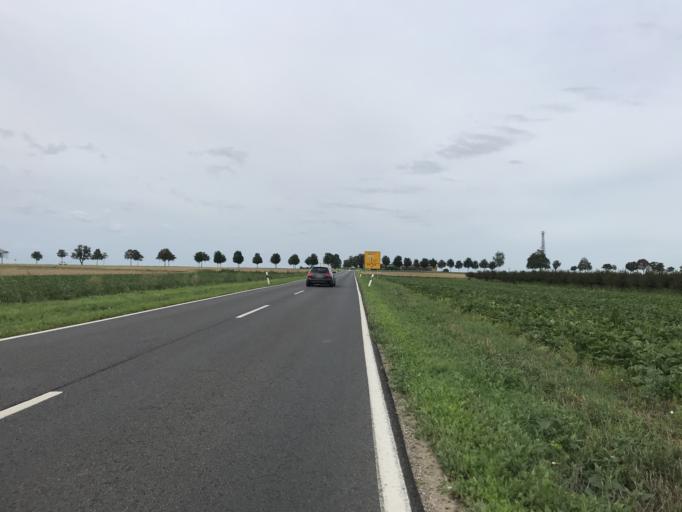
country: DE
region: Rheinland-Pfalz
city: Vendersheim
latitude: 49.8784
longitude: 8.0629
